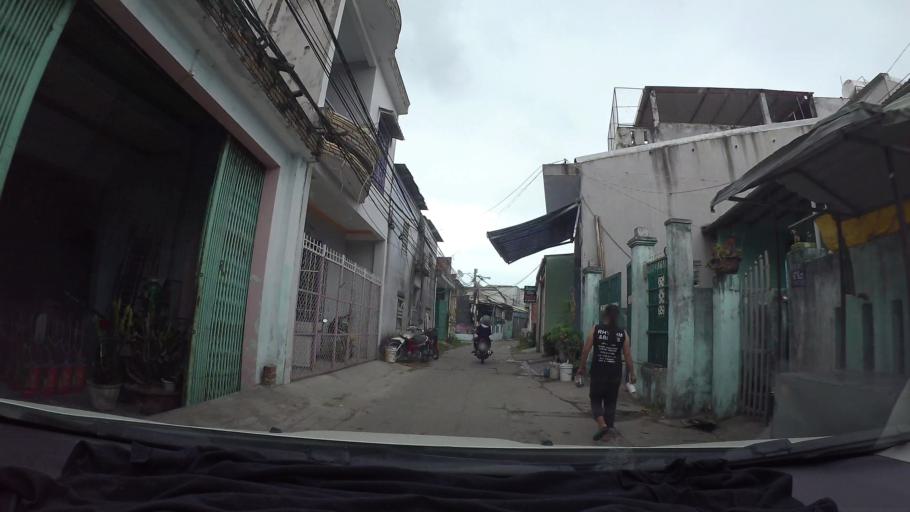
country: VN
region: Da Nang
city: Lien Chieu
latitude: 16.0526
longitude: 108.1577
